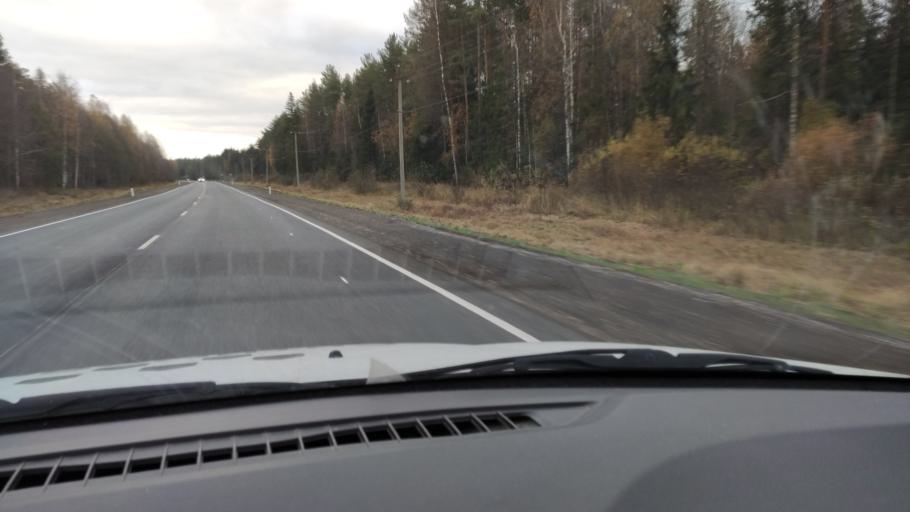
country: RU
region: Kirov
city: Belaya Kholunitsa
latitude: 58.8443
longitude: 50.7670
